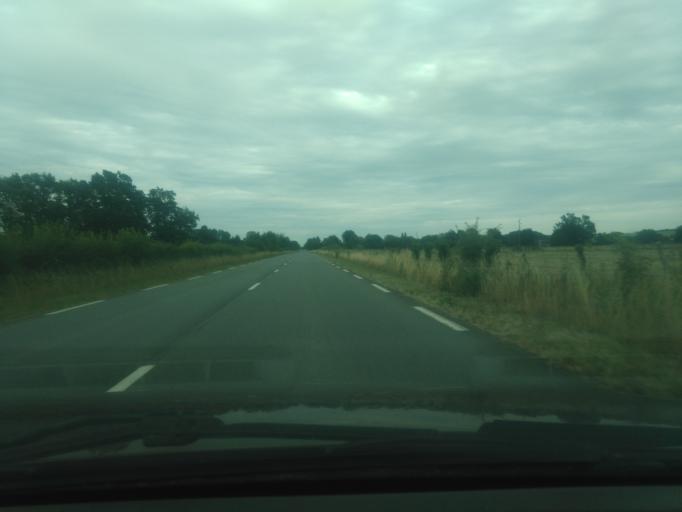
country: FR
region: Centre
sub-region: Departement du Cher
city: Charenton-du-Cher
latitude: 46.7312
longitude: 2.6088
